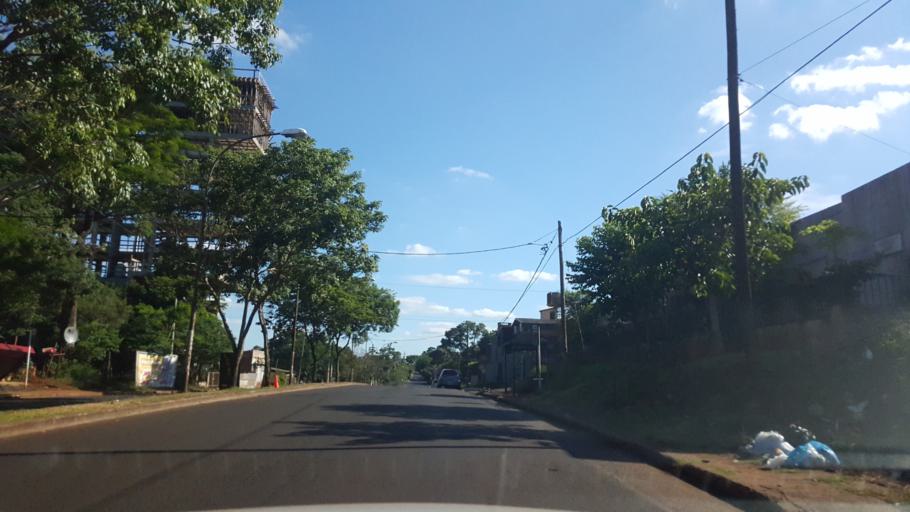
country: AR
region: Misiones
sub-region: Departamento de Capital
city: Posadas
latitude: -27.3927
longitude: -55.8936
